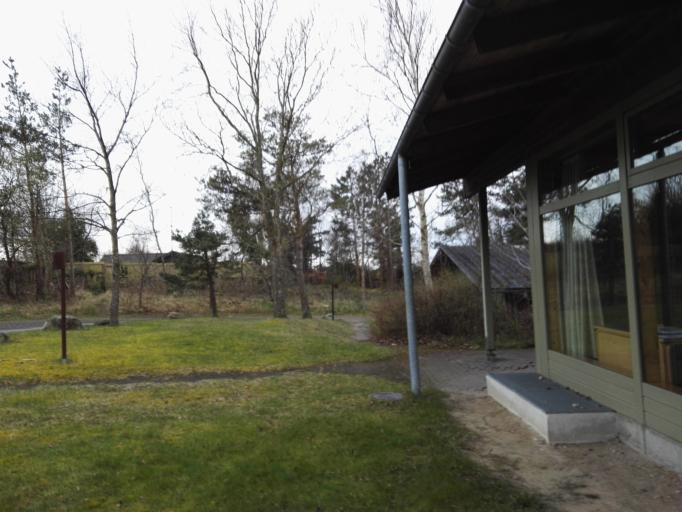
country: DK
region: Capital Region
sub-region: Gribskov Kommune
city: Gilleleje
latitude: 56.1228
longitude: 12.2681
